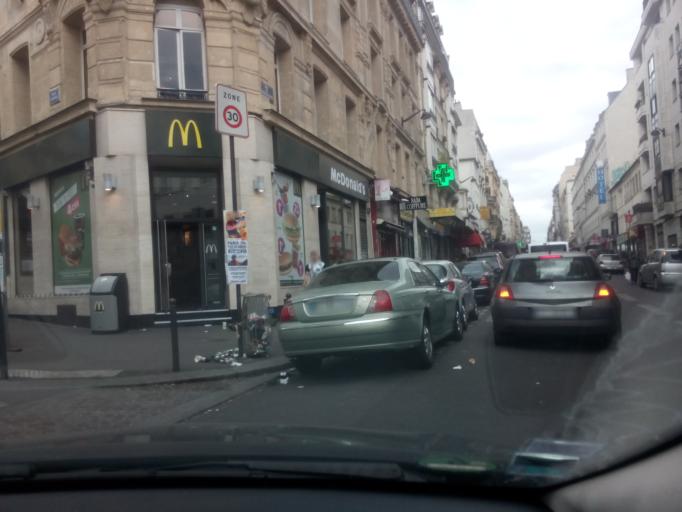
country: FR
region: Ile-de-France
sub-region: Paris
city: Saint-Ouen
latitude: 48.8837
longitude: 2.3470
